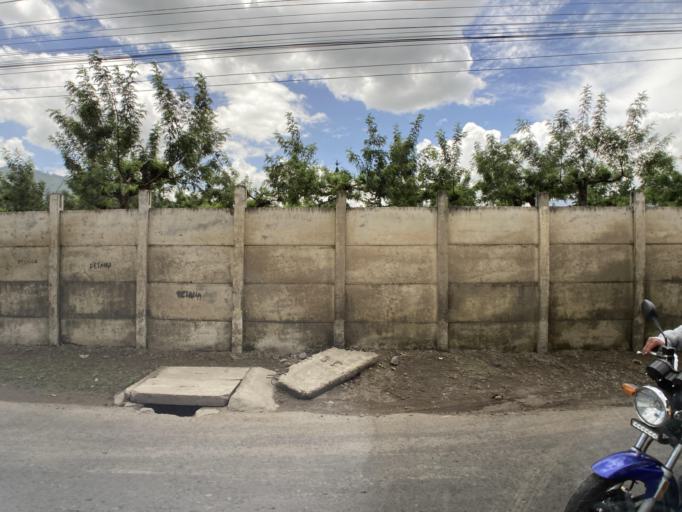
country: GT
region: Sacatepequez
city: Antigua Guatemala
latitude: 14.5516
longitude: -90.7442
